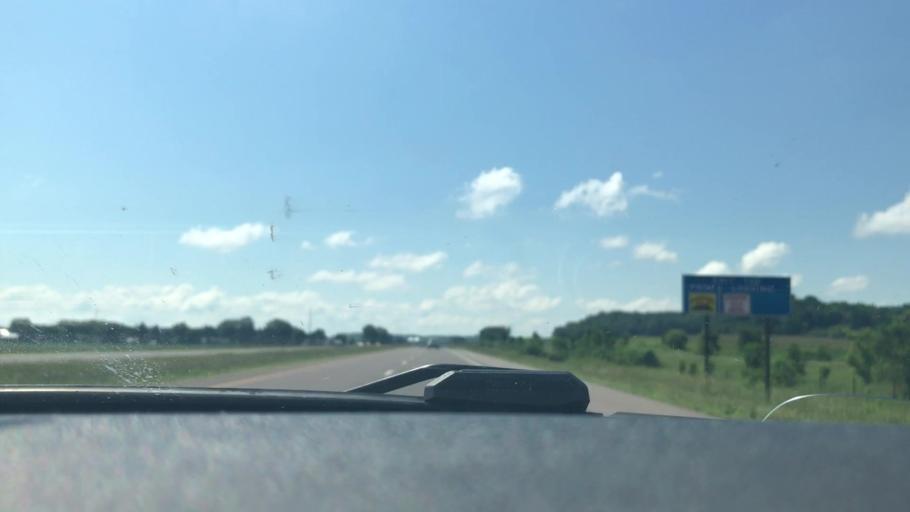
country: US
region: Wisconsin
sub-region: Chippewa County
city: Chippewa Falls
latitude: 45.0125
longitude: -91.4427
